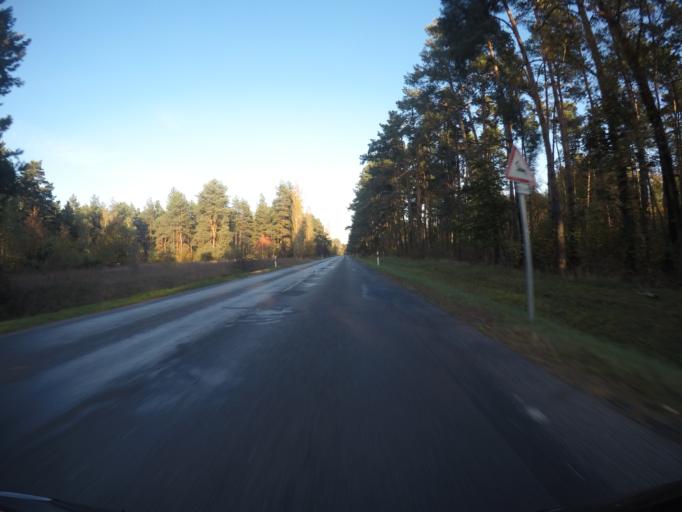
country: HU
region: Somogy
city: Barcs
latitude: 45.9790
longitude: 17.5741
